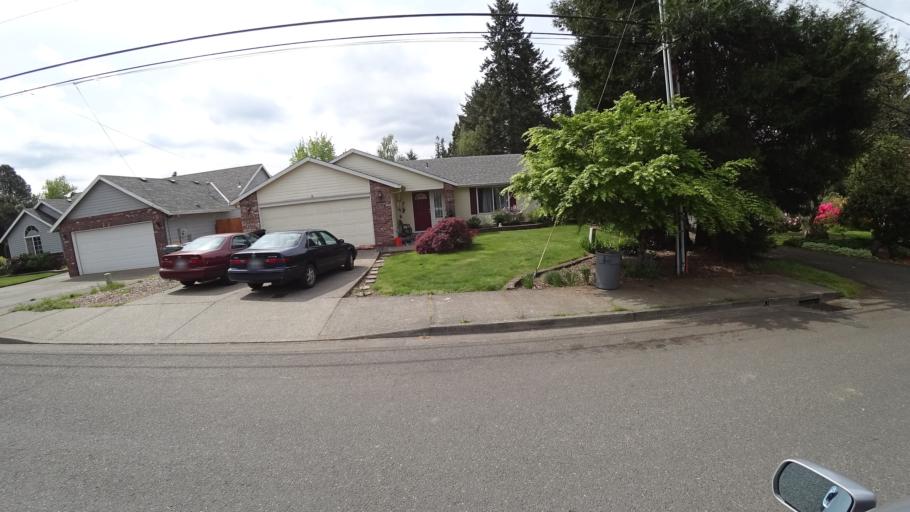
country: US
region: Oregon
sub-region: Washington County
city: Hillsboro
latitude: 45.5253
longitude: -122.9989
